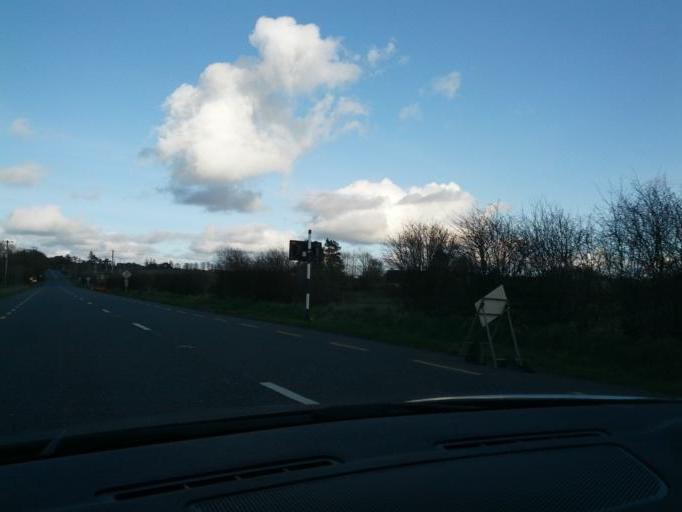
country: IE
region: Connaught
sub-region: Roscommon
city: Castlerea
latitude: 53.6861
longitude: -8.3904
